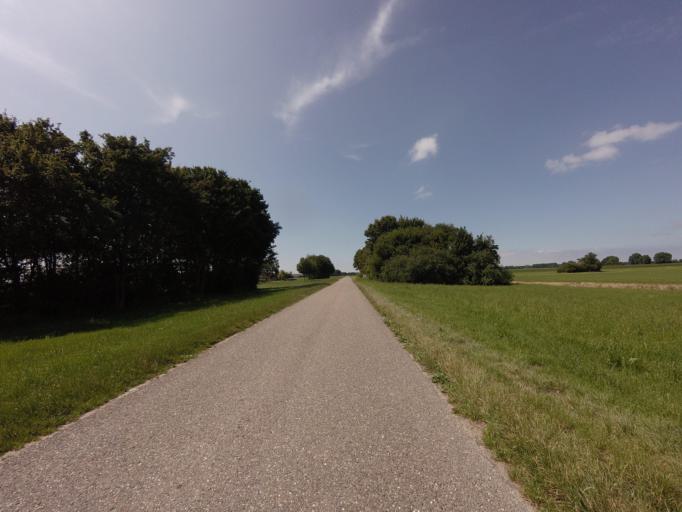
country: NL
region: Flevoland
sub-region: Gemeente Lelystad
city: Lelystad
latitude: 52.4344
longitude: 5.4707
